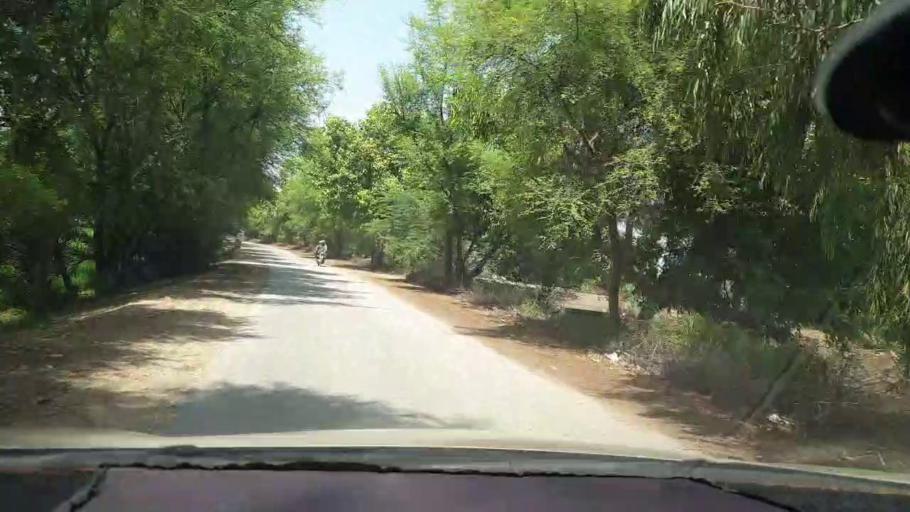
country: PK
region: Sindh
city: Kambar
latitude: 27.6561
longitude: 67.9607
